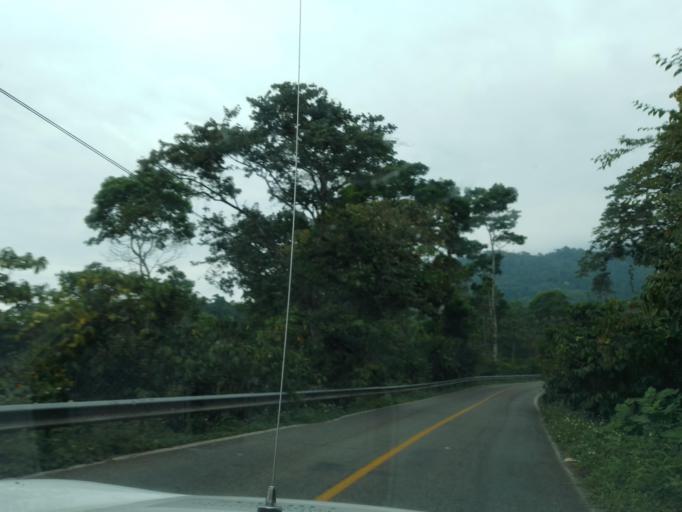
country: MX
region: Chiapas
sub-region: Union Juarez
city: Santo Domingo
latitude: 15.0414
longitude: -92.1348
